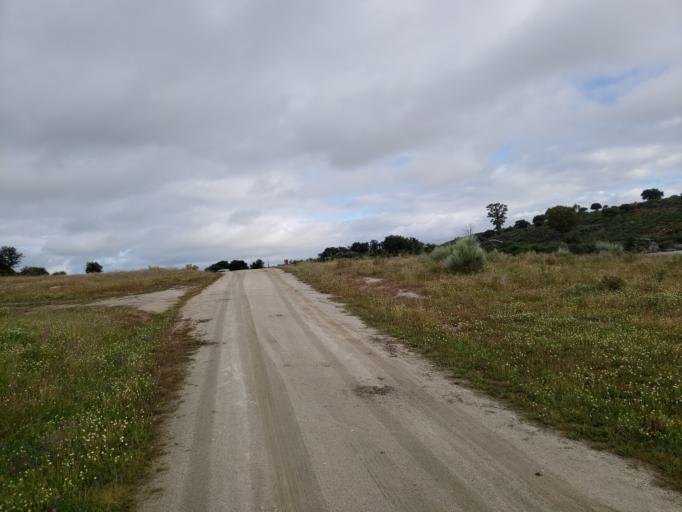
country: ES
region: Extremadura
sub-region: Provincia de Caceres
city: Malpartida de Caceres
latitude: 39.4245
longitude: -6.4869
